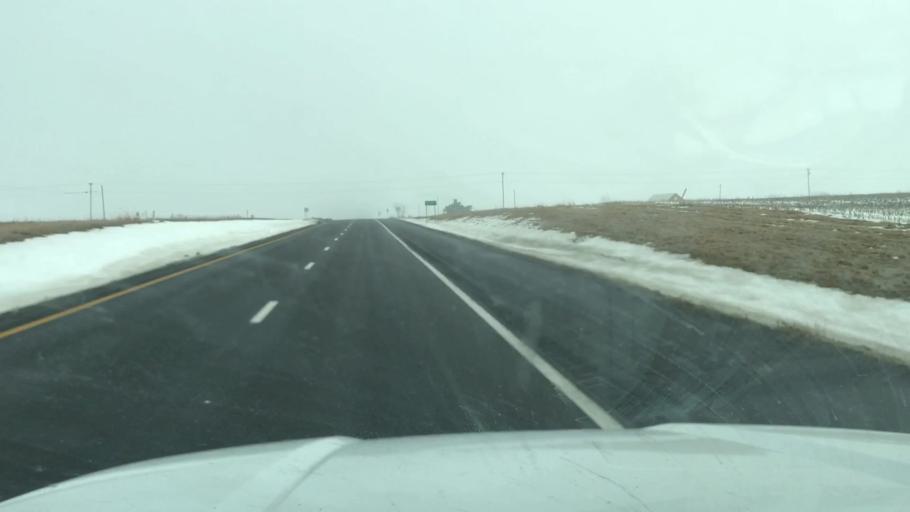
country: US
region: Missouri
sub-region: DeKalb County
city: Maysville
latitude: 39.7620
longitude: -94.4344
